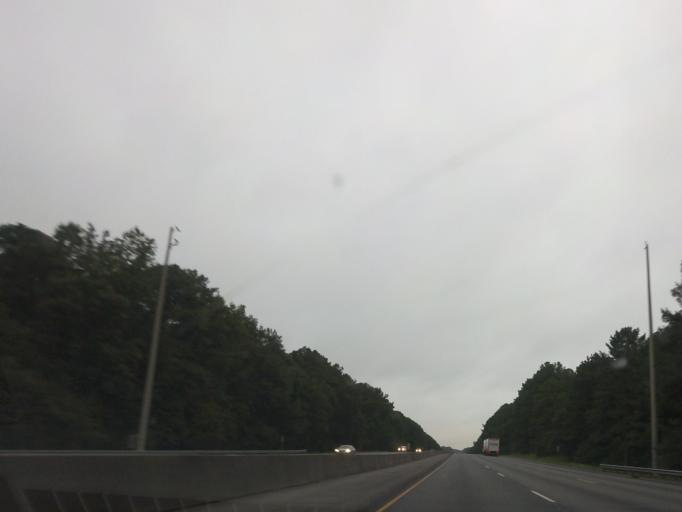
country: US
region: Georgia
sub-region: Bibb County
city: West Point
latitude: 32.8907
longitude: -83.7785
